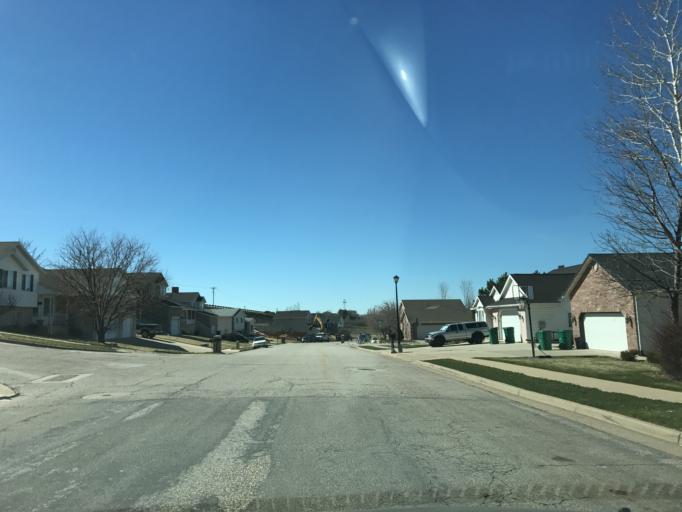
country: US
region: Utah
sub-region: Davis County
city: South Weber
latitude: 41.1058
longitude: -111.9245
